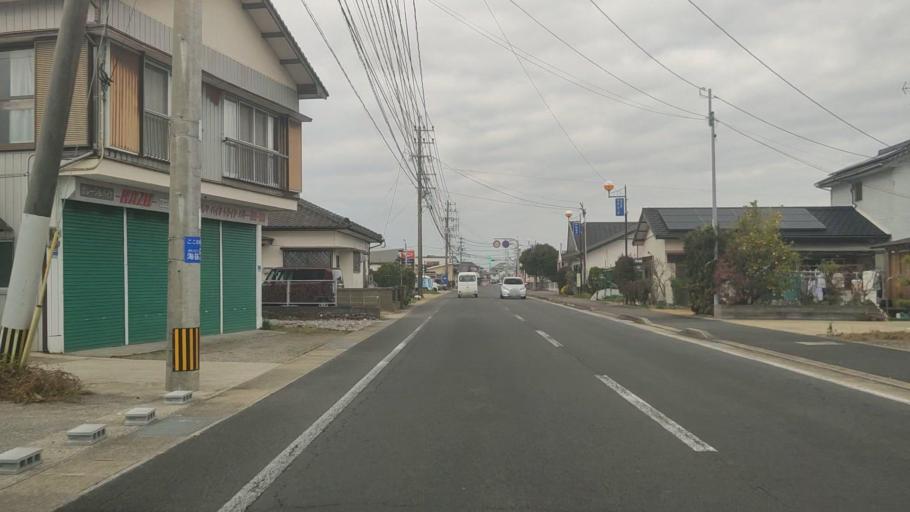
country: JP
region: Nagasaki
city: Shimabara
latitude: 32.8644
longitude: 130.3222
